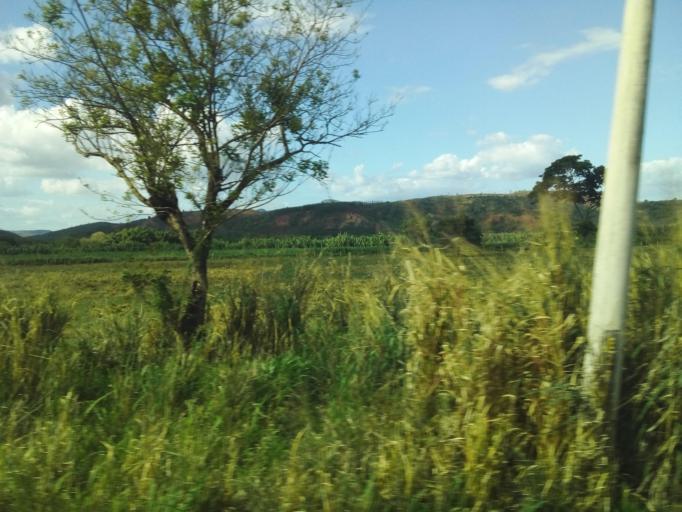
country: BR
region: Minas Gerais
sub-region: Conselheiro Pena
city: Conselheiro Pena
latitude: -18.9846
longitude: -41.6047
